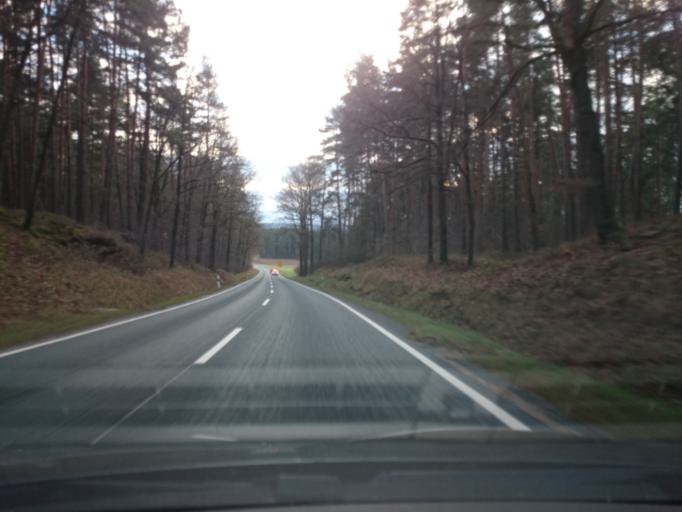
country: DE
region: Bavaria
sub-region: Regierungsbezirk Mittelfranken
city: Hilpoltstein
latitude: 49.1745
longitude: 11.1805
